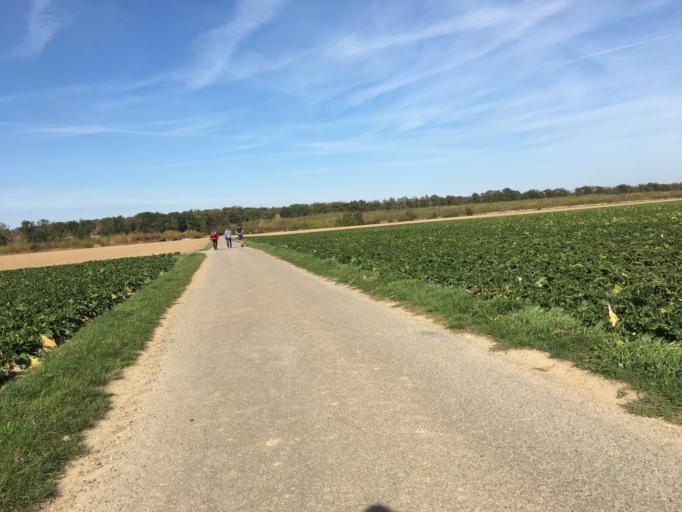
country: DE
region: North Rhine-Westphalia
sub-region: Regierungsbezirk Koln
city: Merzenich
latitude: 50.8418
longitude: 6.5336
